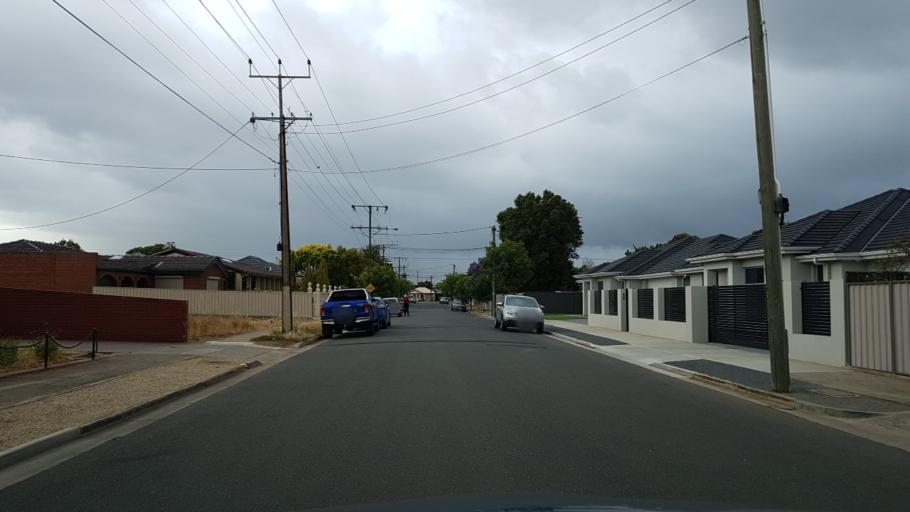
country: AU
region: South Australia
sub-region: City of West Torrens
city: Plympton
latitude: -34.9603
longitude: 138.5500
